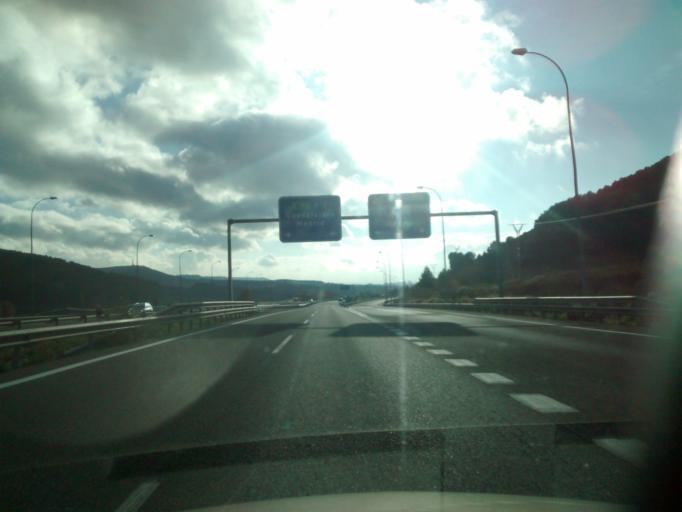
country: ES
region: Castille-La Mancha
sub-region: Provincia de Guadalajara
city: Tortola de Henares
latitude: 40.6682
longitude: -3.1068
